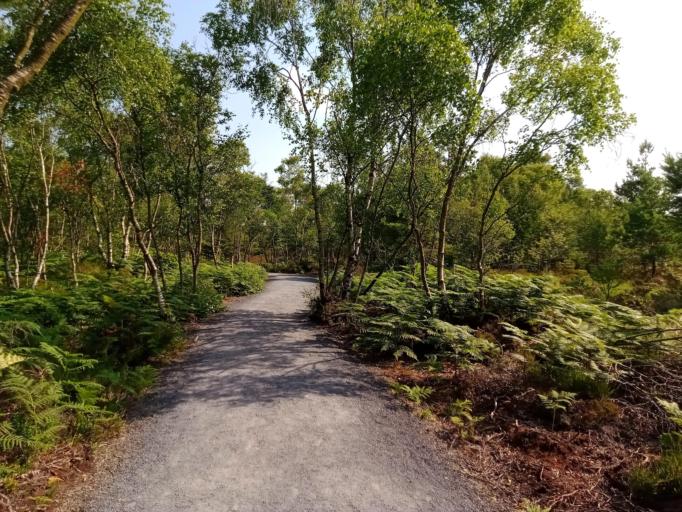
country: IE
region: Leinster
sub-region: Laois
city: Abbeyleix
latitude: 52.9009
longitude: -7.3530
